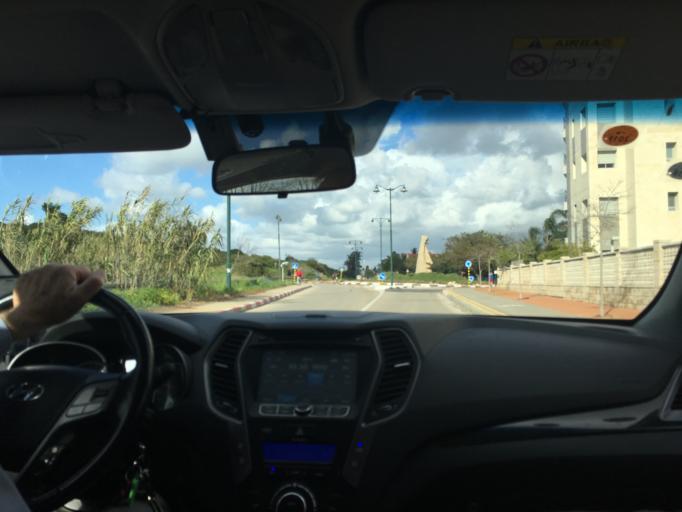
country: IL
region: Central District
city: Ness Ziona
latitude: 31.9321
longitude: 34.7861
